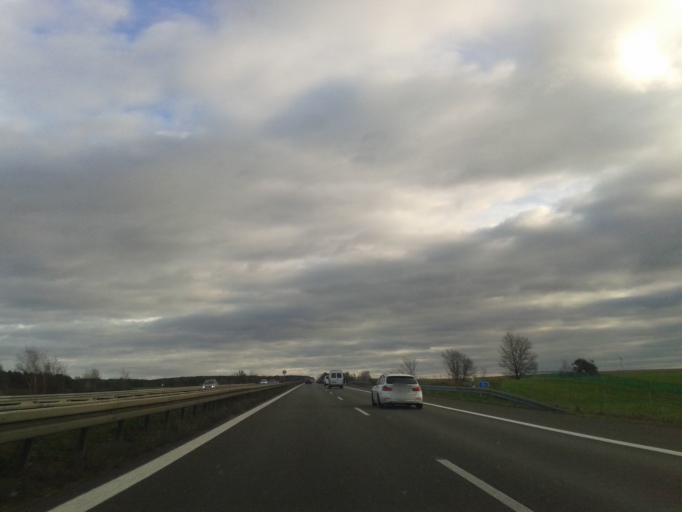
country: DE
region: Saxony
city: Wachau
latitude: 51.1710
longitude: 13.8888
